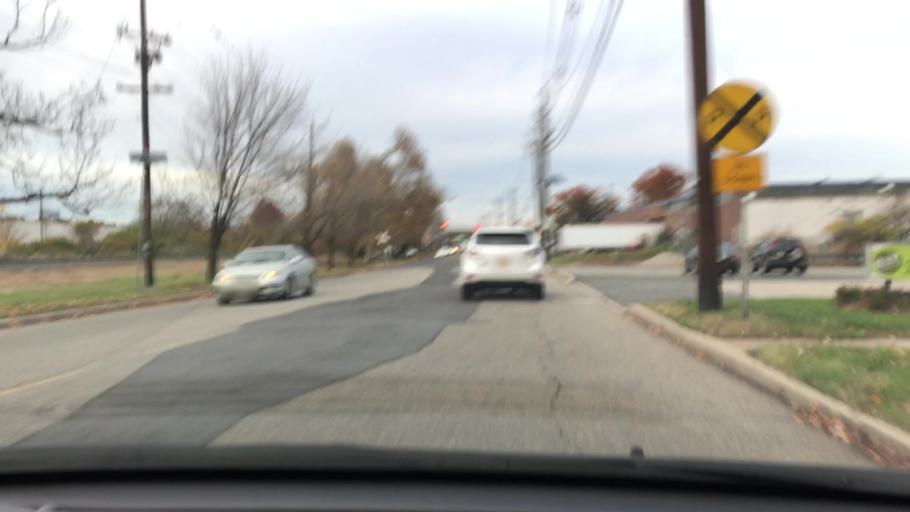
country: US
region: New Jersey
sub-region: Bergen County
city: Hasbrouck Heights
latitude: 40.8672
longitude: -74.0605
